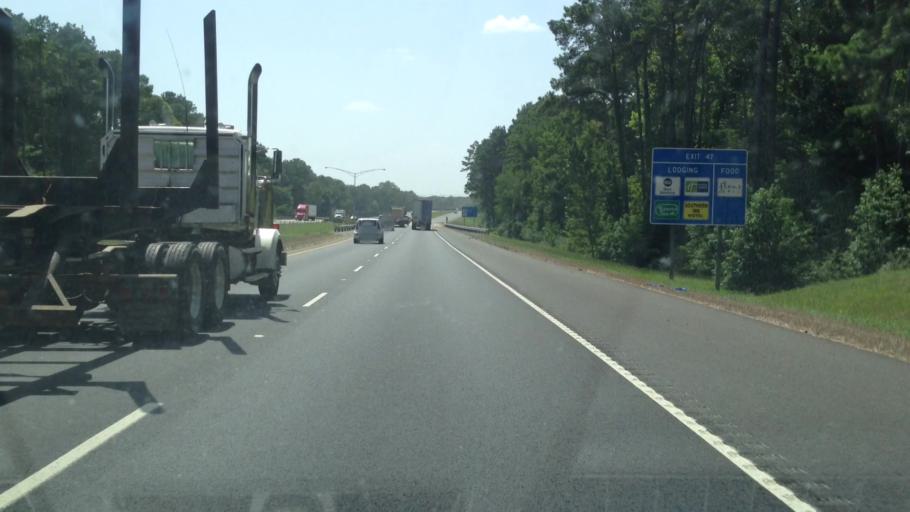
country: US
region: Louisiana
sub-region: Webster Parish
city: Minden
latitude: 32.5878
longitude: -93.2825
